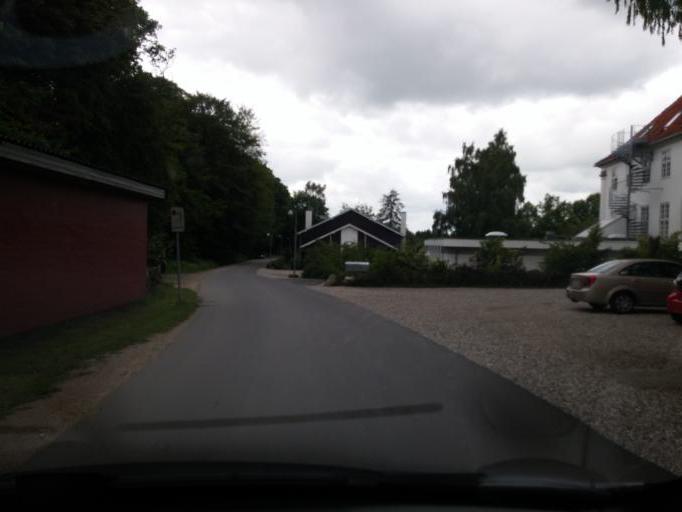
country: DK
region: Capital Region
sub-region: Hillerod Kommune
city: Hillerod
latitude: 55.9443
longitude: 12.3100
